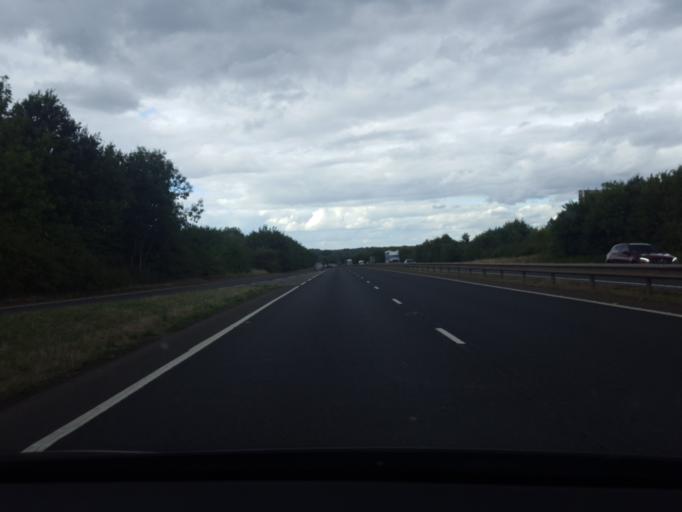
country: GB
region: England
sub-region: Leicestershire
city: Mountsorrel
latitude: 52.7211
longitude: -1.1281
